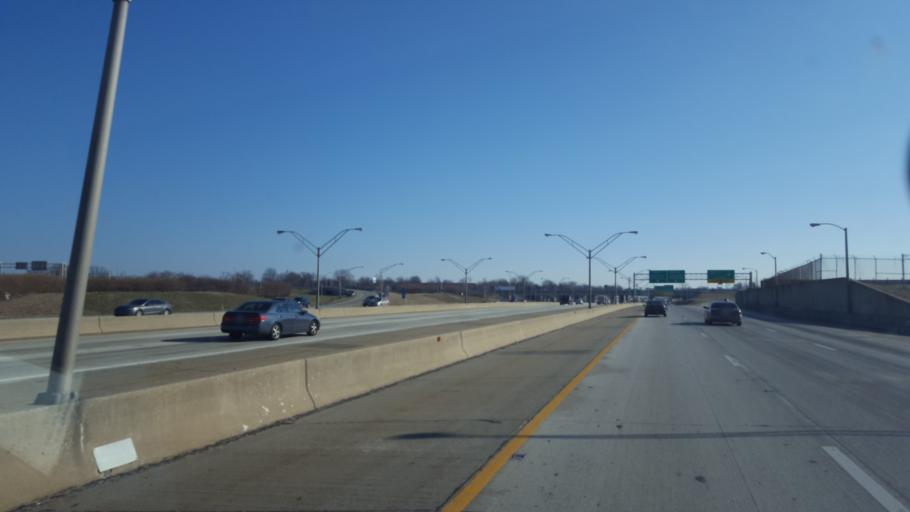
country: US
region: Kentucky
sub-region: Jefferson County
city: Audubon Park
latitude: 38.1897
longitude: -85.7354
